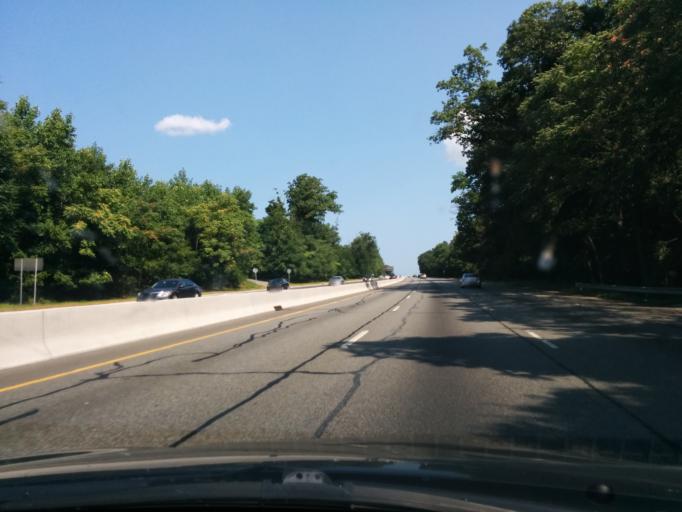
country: US
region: New Jersey
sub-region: Bergen County
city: Saddle River
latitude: 41.0365
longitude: -74.1123
